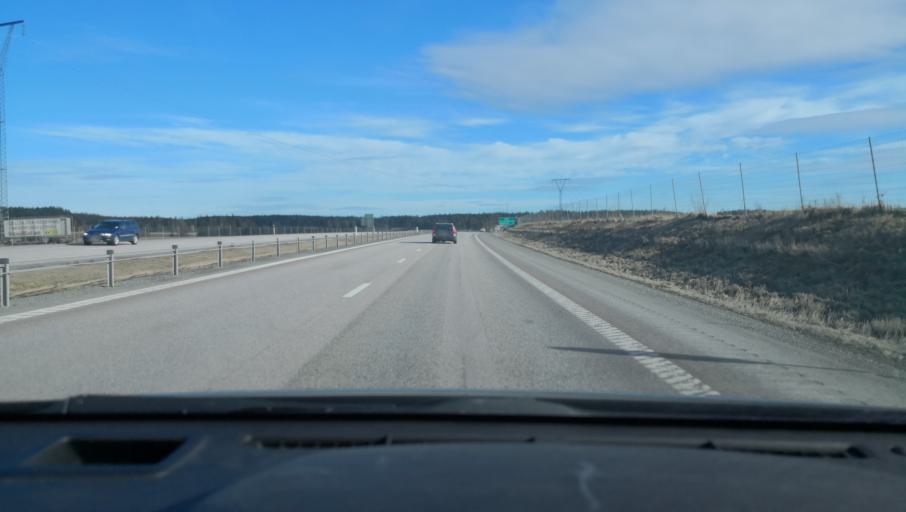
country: SE
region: Uppsala
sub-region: Enkopings Kommun
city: Hummelsta
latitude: 59.6322
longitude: 16.8491
